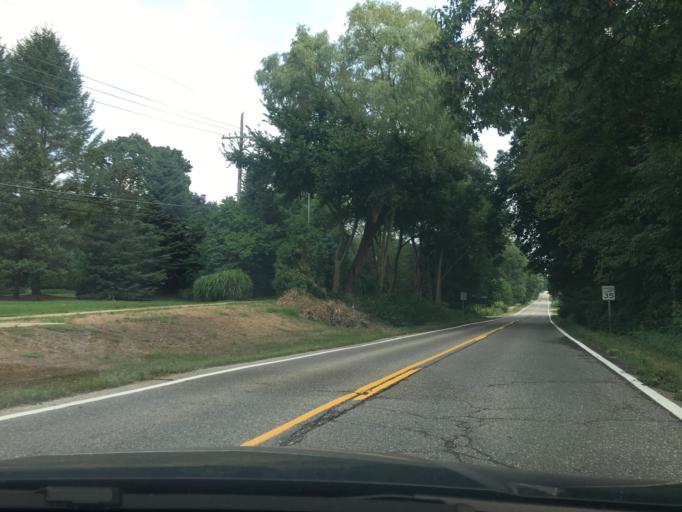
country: US
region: Michigan
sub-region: Oakland County
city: Bloomfield Hills
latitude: 42.5754
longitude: -83.2179
